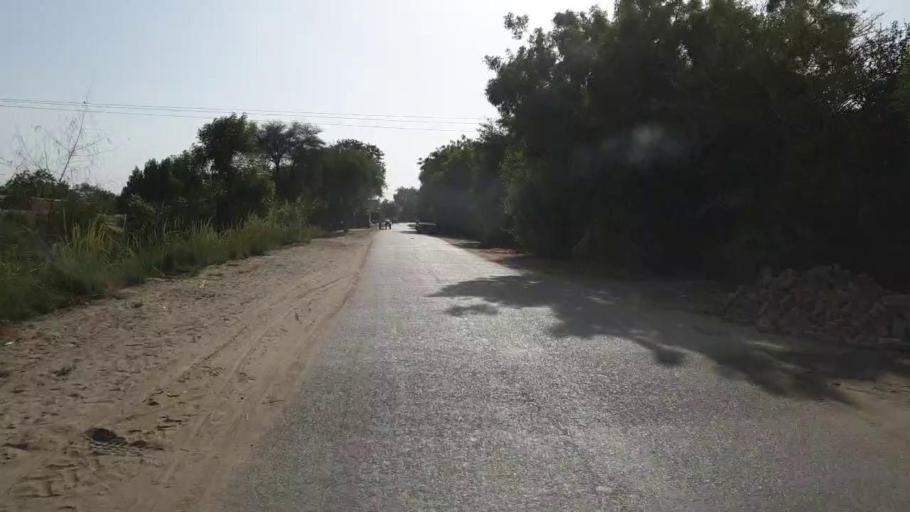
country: PK
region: Sindh
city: Daur
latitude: 26.4753
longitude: 68.4714
